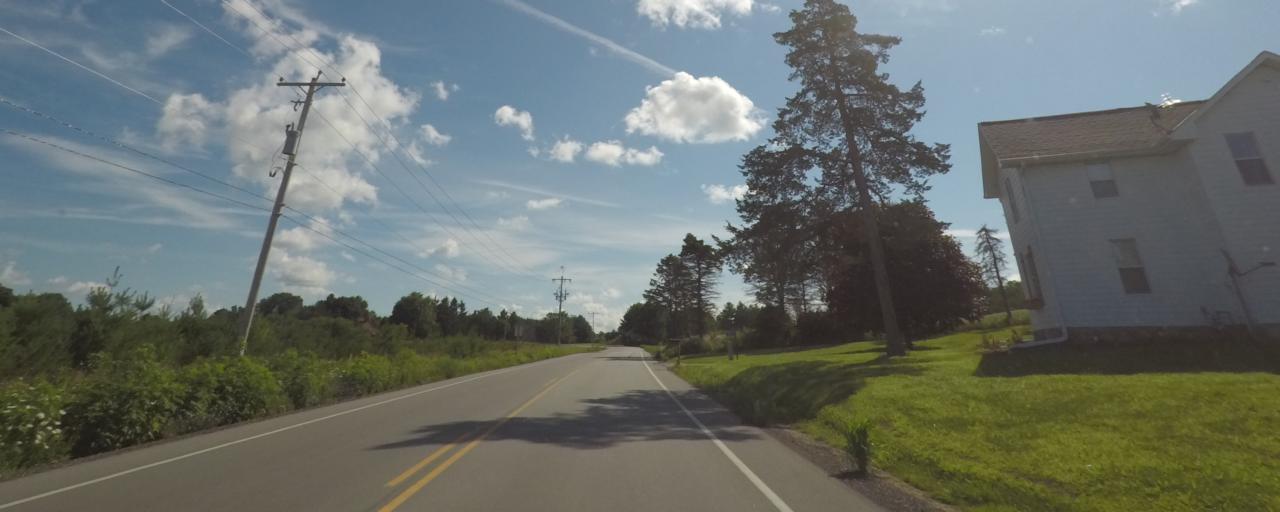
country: US
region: Wisconsin
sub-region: Waukesha County
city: Oconomowoc
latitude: 43.0775
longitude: -88.5428
